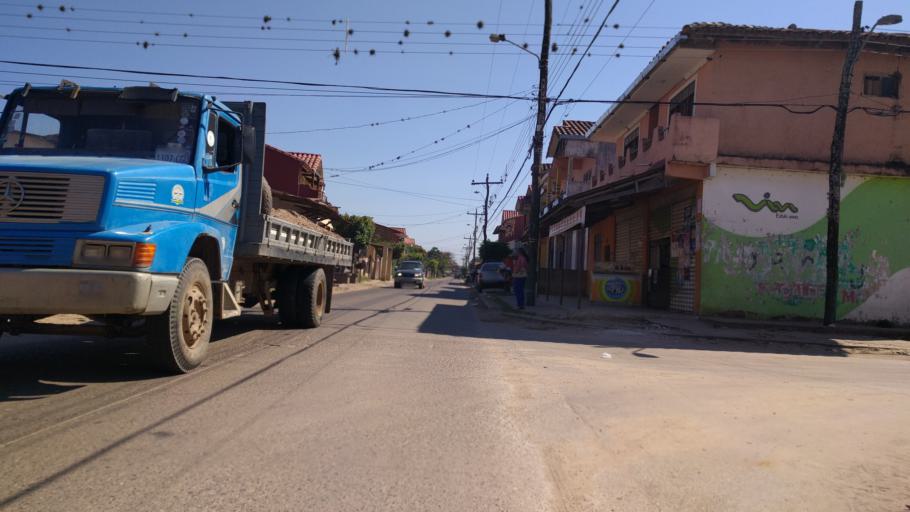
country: BO
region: Santa Cruz
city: Santa Cruz de la Sierra
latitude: -17.8318
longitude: -63.2257
